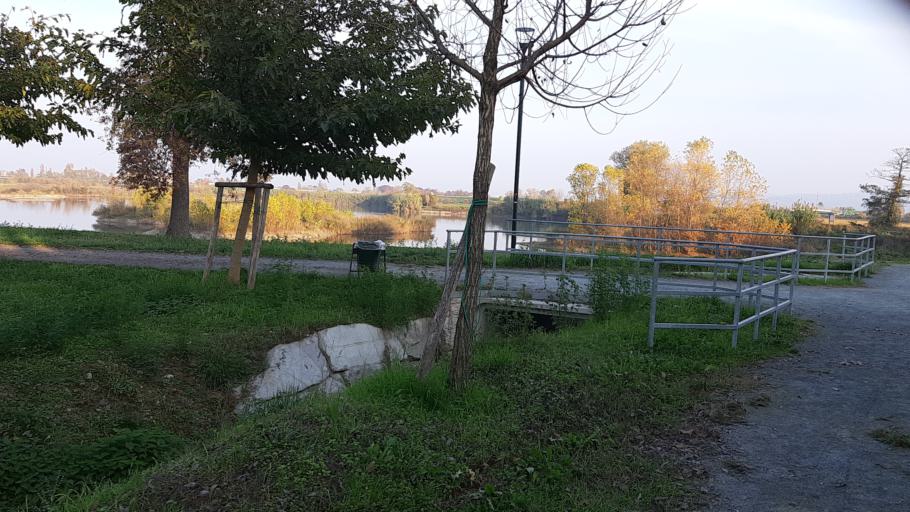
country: IT
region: Piedmont
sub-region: Provincia di Torino
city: Settimo Torinese
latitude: 45.1311
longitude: 7.7166
